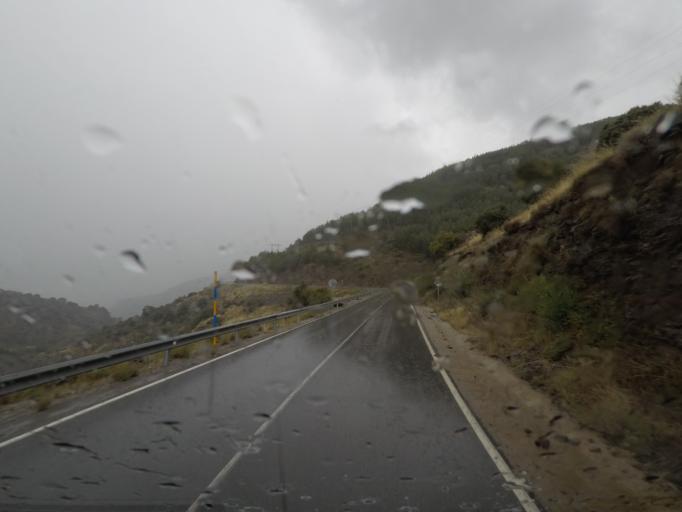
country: ES
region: Andalusia
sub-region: Provincia de Almeria
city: Bayarcal
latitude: 37.0667
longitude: -3.0169
